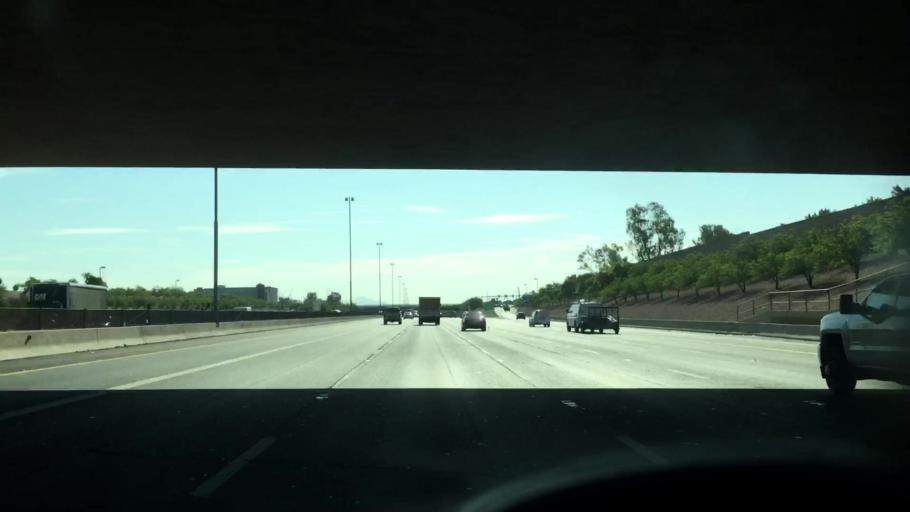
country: US
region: Arizona
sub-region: Maricopa County
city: San Carlos
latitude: 33.3854
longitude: -111.8636
